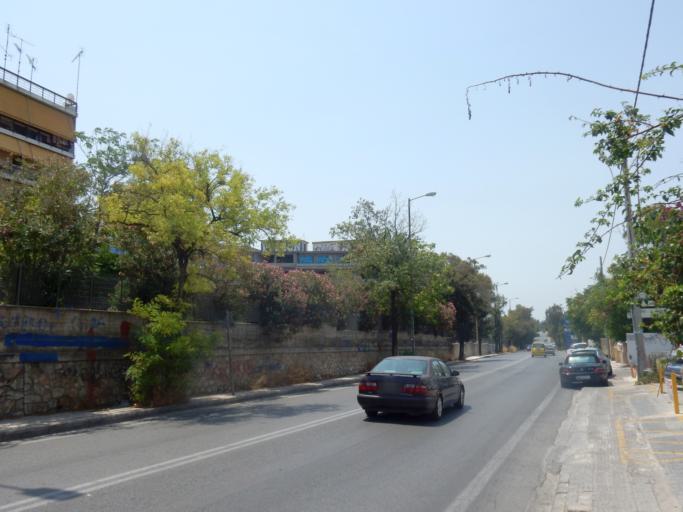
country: GR
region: Attica
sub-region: Nomarchia Athinas
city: Nea Filadelfeia
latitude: 38.0326
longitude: 23.7439
